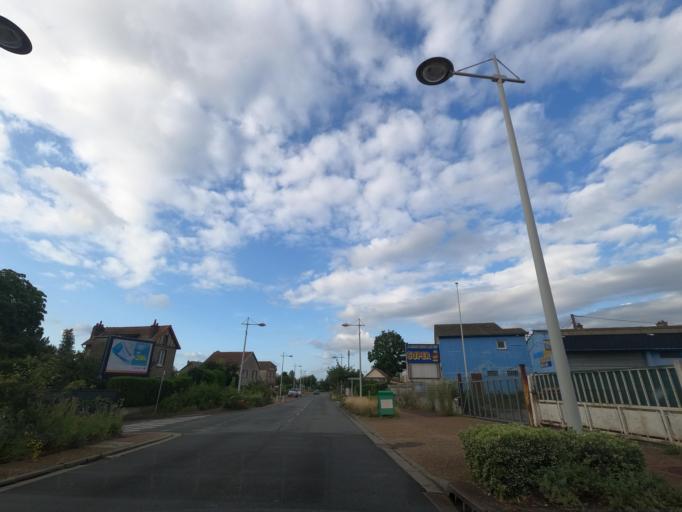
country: FR
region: Haute-Normandie
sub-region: Departement de la Seine-Maritime
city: Grand-Couronne
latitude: 49.3630
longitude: 1.0130
